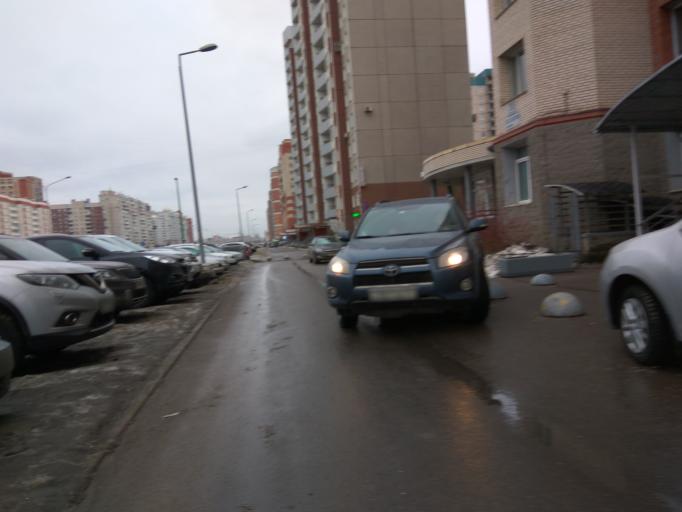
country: RU
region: St.-Petersburg
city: Staraya Derevnya
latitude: 60.0028
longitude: 30.2392
